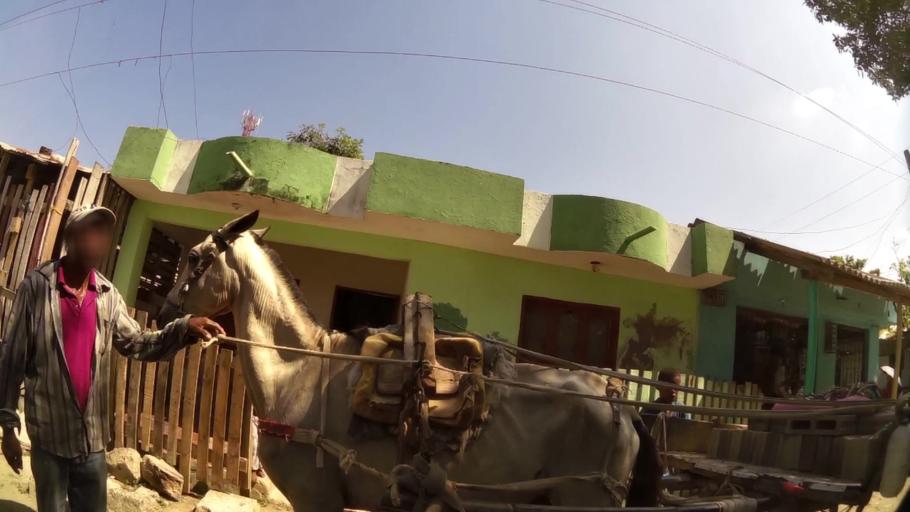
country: CO
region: Bolivar
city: Cartagena
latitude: 10.3561
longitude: -75.4859
